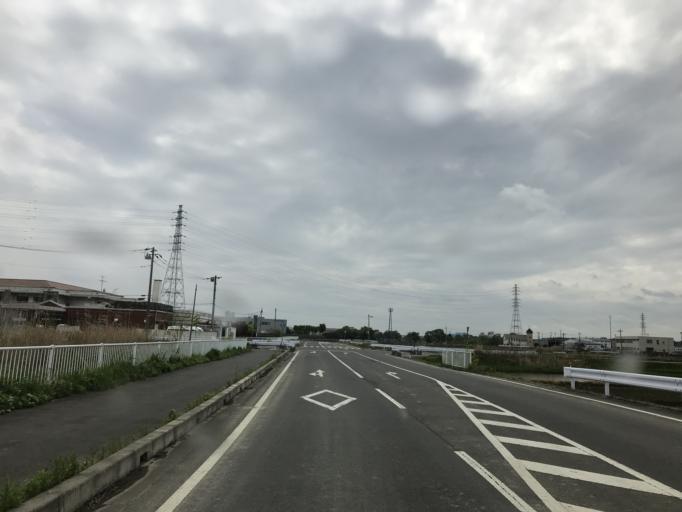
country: JP
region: Ibaraki
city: Mitsukaido
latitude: 36.0085
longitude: 139.9842
